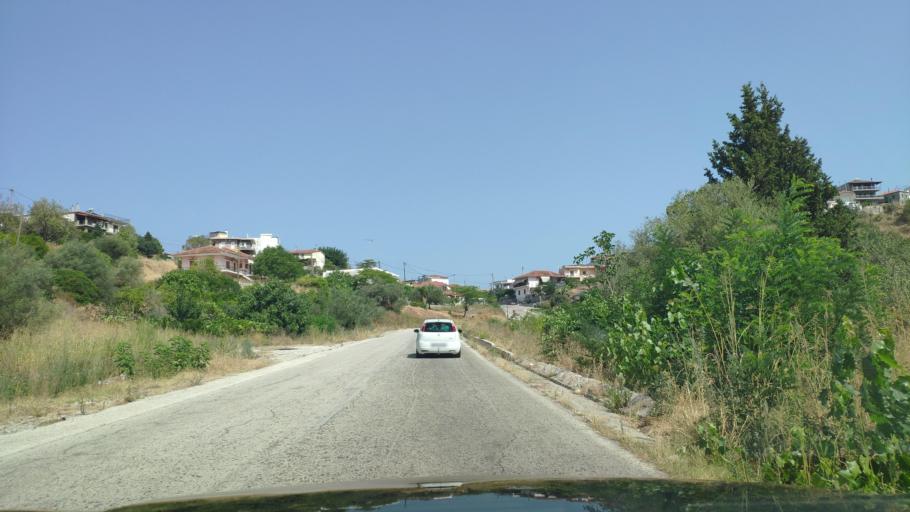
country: GR
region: Epirus
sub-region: Nomos Artas
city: Peta
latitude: 39.1632
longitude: 21.0356
